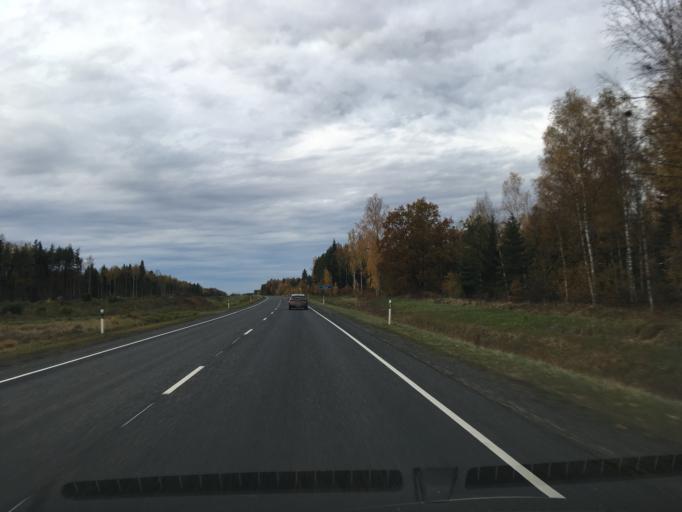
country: EE
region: Harju
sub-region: Nissi vald
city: Turba
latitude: 58.9499
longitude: 24.0828
